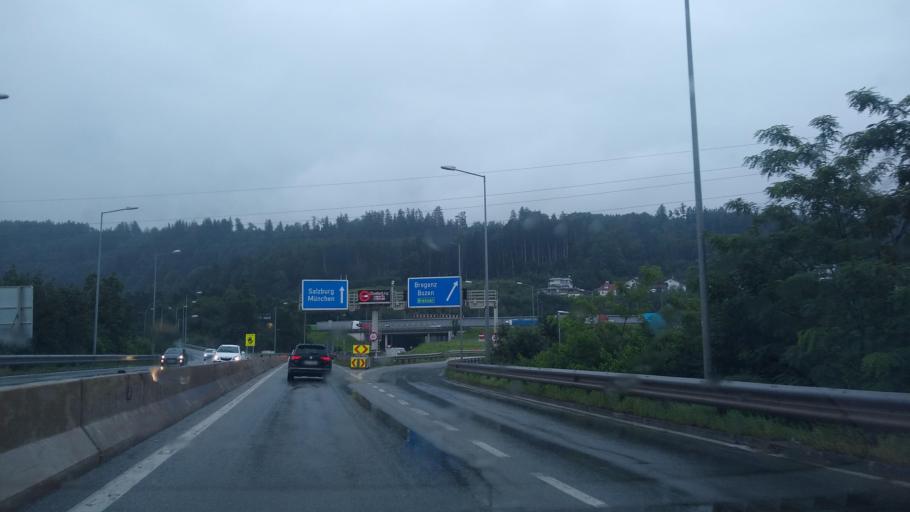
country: AT
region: Tyrol
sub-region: Politischer Bezirk Innsbruck Land
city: Ampass
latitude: 47.2628
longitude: 11.4368
